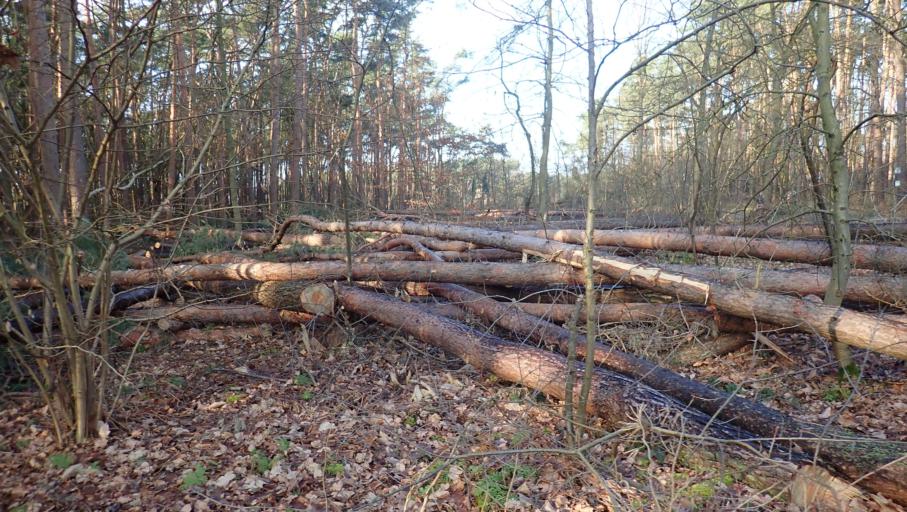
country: BE
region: Flanders
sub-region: Provincie Vlaams-Brabant
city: Tremelo
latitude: 51.0062
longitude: 4.7351
